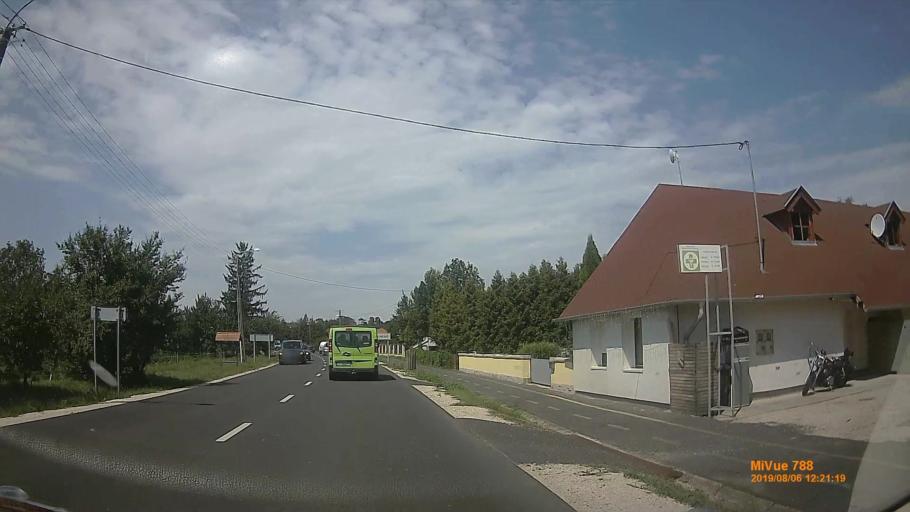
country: HU
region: Vas
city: Taplanszentkereszt
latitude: 47.1841
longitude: 16.7437
